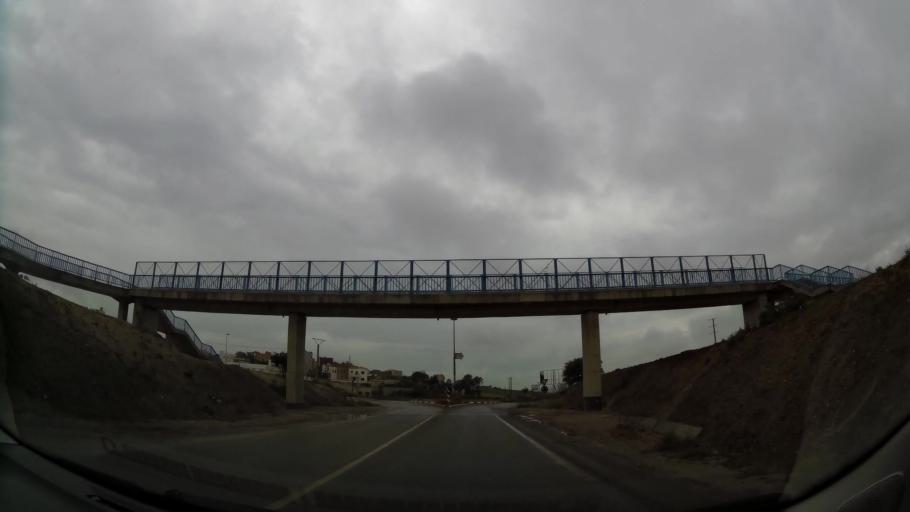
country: MA
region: Oriental
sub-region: Nador
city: Nador
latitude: 35.1541
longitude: -3.0229
